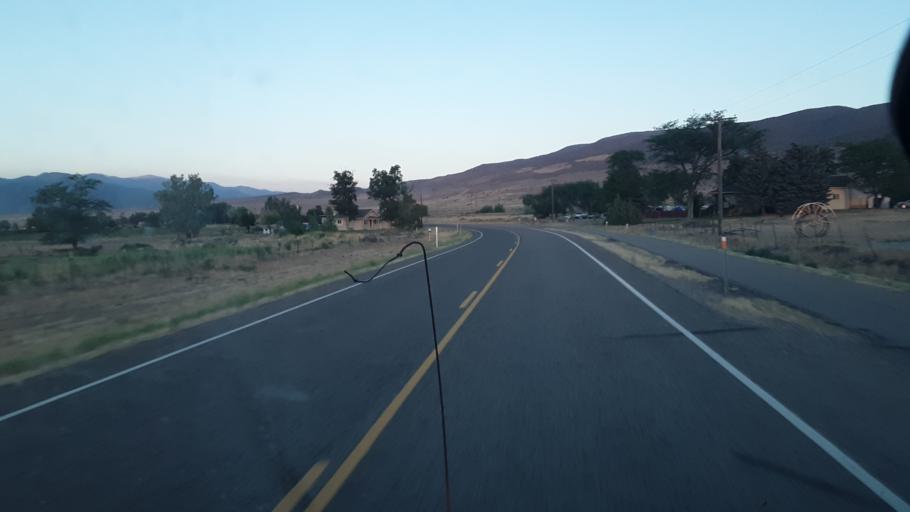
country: US
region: Utah
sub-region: Sevier County
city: Monroe
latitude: 38.6515
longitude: -112.2069
